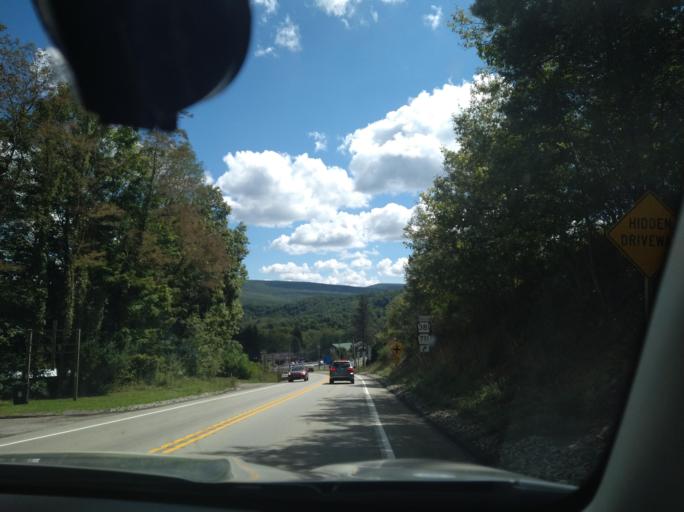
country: US
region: Pennsylvania
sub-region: Fayette County
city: Bear Rocks
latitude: 40.0929
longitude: -79.3498
